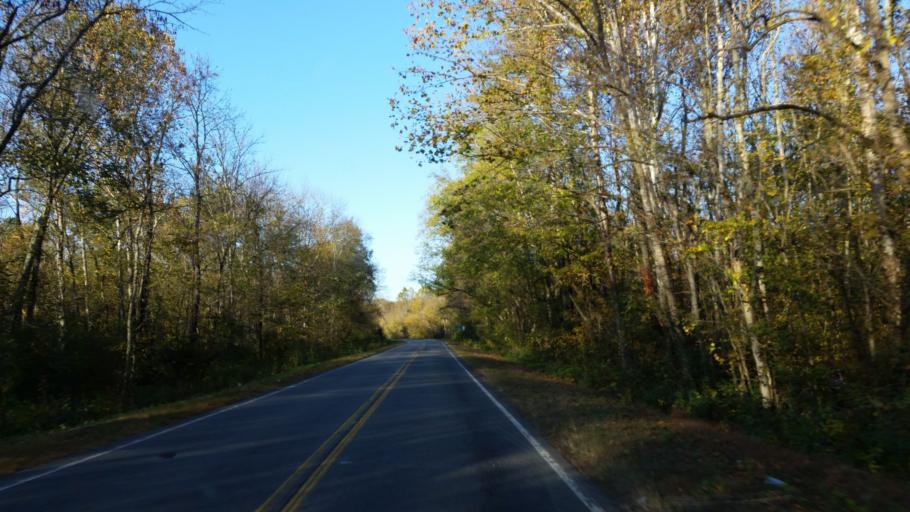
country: US
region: Georgia
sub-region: Bartow County
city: Adairsville
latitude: 34.2682
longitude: -84.9579
